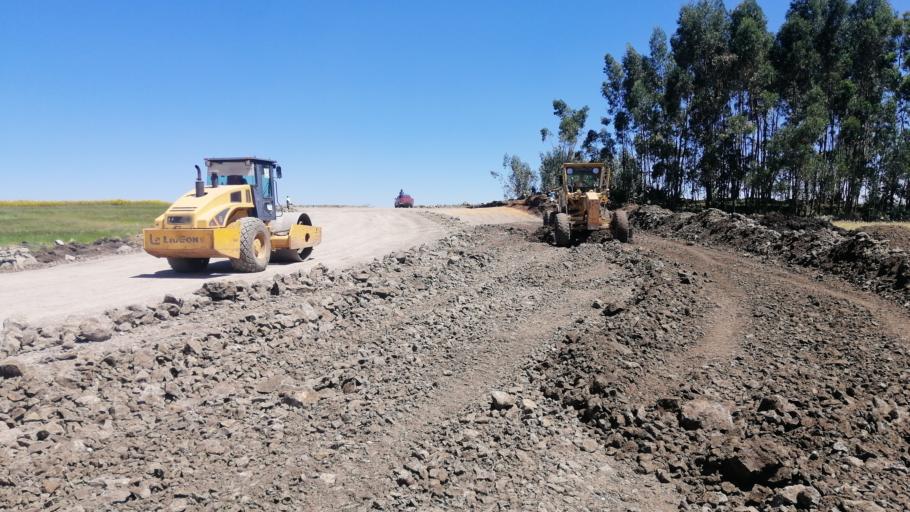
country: ET
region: Amhara
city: Debre Tabor
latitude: 11.4189
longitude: 38.2188
